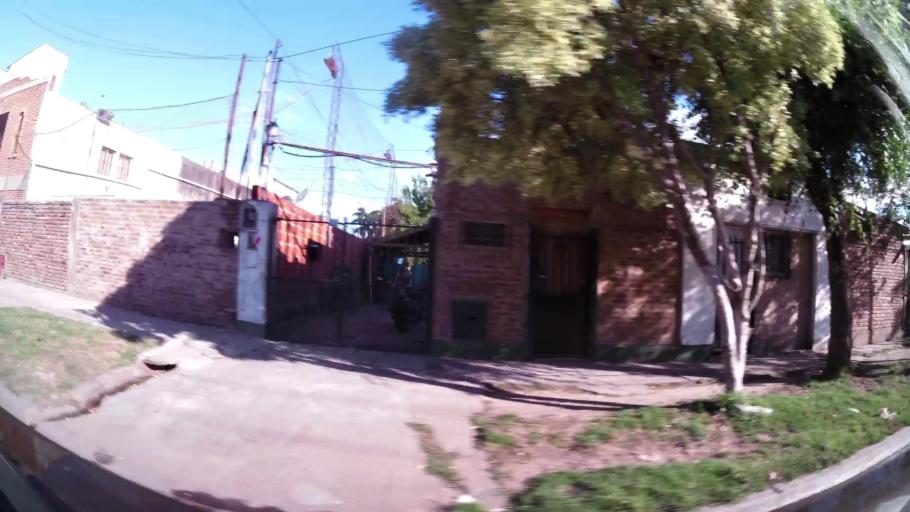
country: AR
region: Buenos Aires
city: Santa Catalina - Dique Lujan
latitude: -34.4895
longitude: -58.7248
